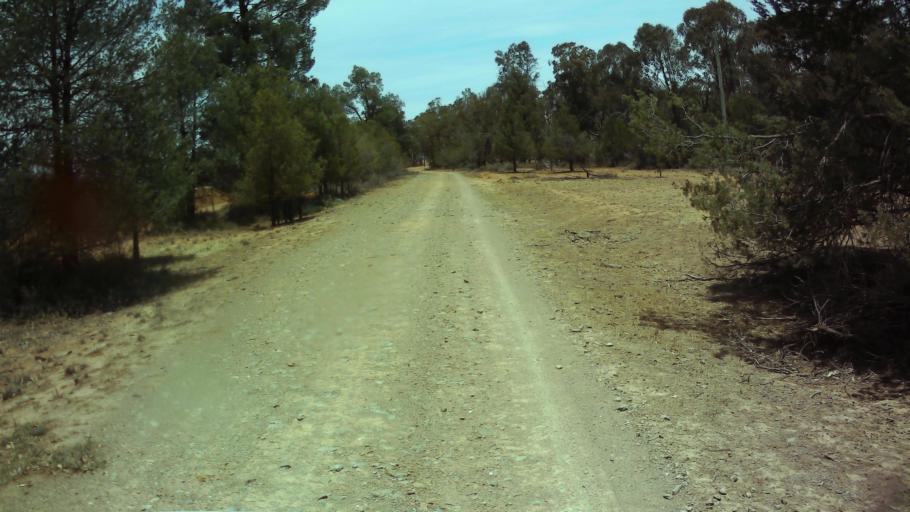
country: AU
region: New South Wales
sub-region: Weddin
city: Grenfell
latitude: -33.8429
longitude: 147.7253
